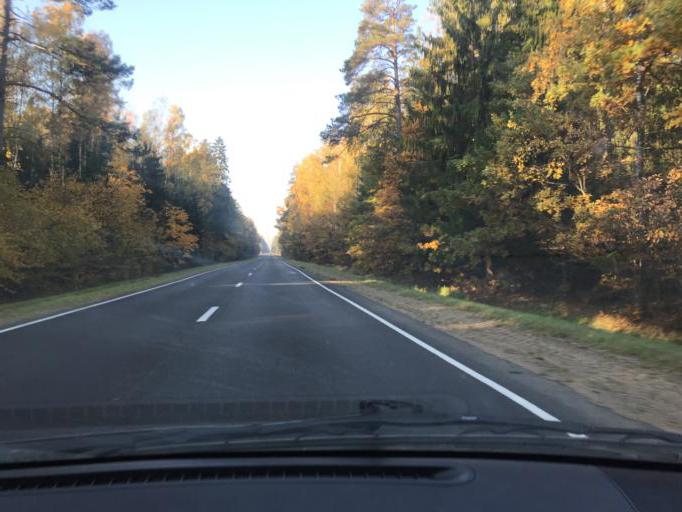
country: BY
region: Brest
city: Tsyelyakhany
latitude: 52.8739
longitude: 25.7342
